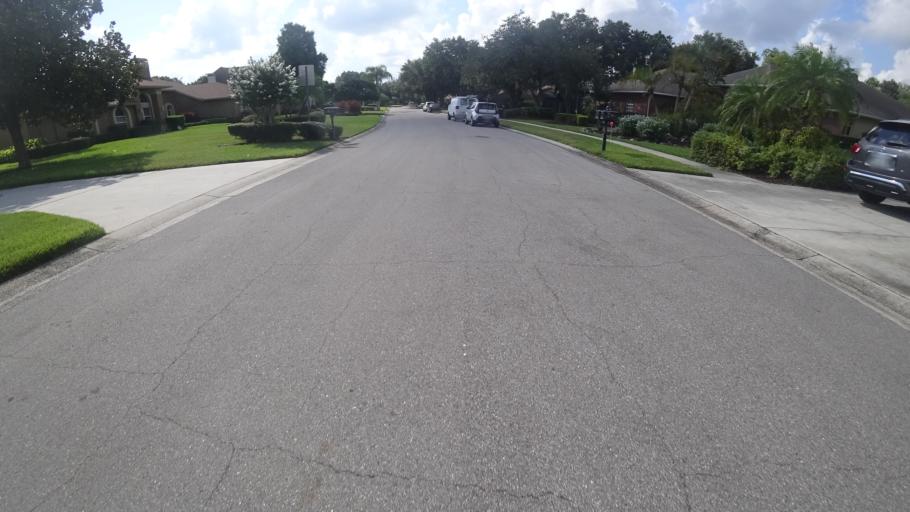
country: US
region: Florida
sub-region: Sarasota County
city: The Meadows
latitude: 27.4254
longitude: -82.4383
